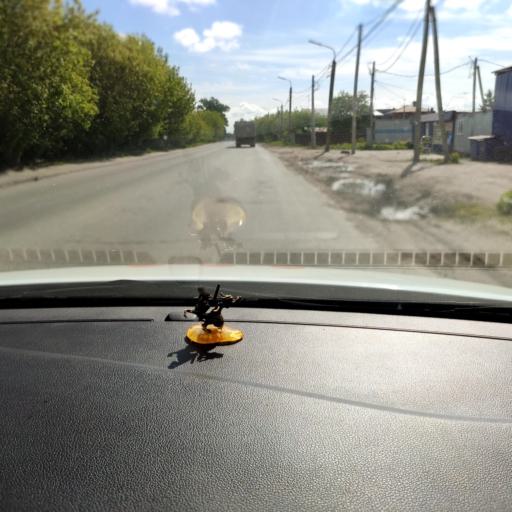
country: RU
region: Tatarstan
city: Staroye Arakchino
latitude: 55.7998
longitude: 49.0126
